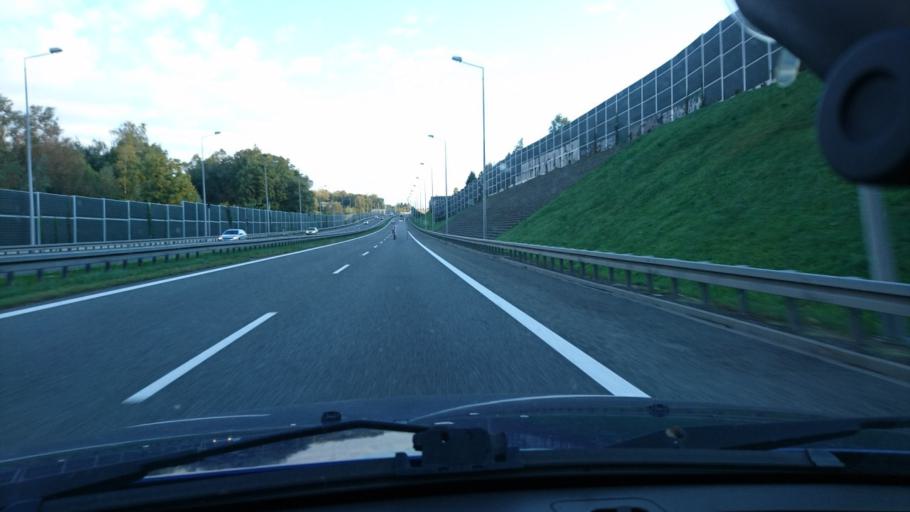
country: PL
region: Silesian Voivodeship
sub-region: Bielsko-Biala
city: Bielsko-Biala
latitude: 49.8340
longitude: 19.0857
